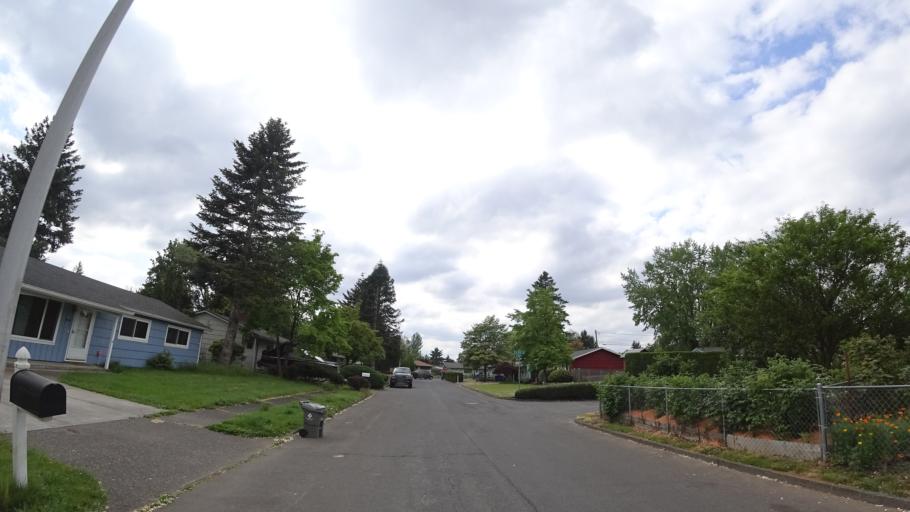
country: US
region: Oregon
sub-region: Multnomah County
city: Gresham
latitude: 45.5057
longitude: -122.4791
